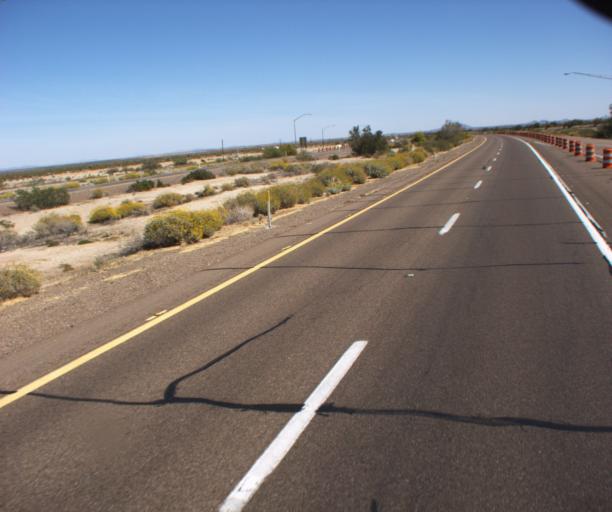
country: US
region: Arizona
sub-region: Yuma County
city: Wellton
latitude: 32.7309
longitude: -113.7147
